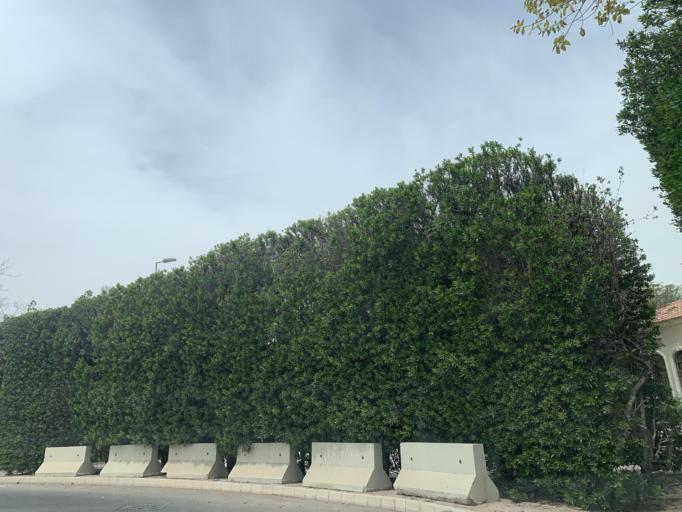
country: BH
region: Northern
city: Ar Rifa'
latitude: 26.1375
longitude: 50.5486
